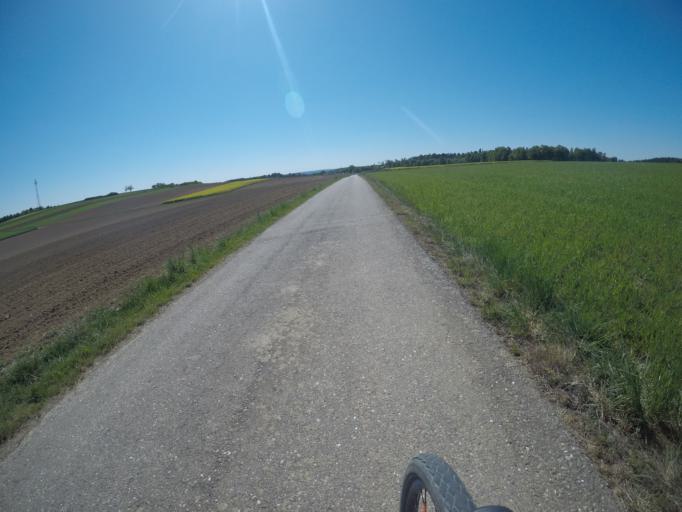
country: DE
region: Baden-Wuerttemberg
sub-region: Karlsruhe Region
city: Heimsheim
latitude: 48.8288
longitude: 8.8914
